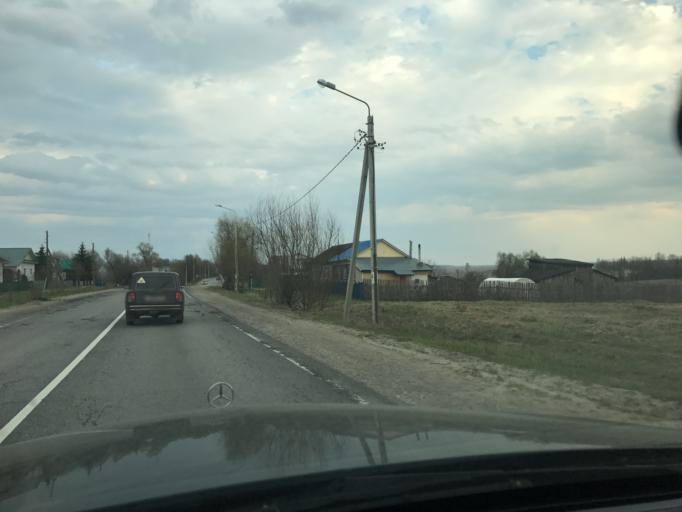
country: RU
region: Vladimir
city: Krasnaya Gorbatka
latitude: 55.6887
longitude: 41.7599
